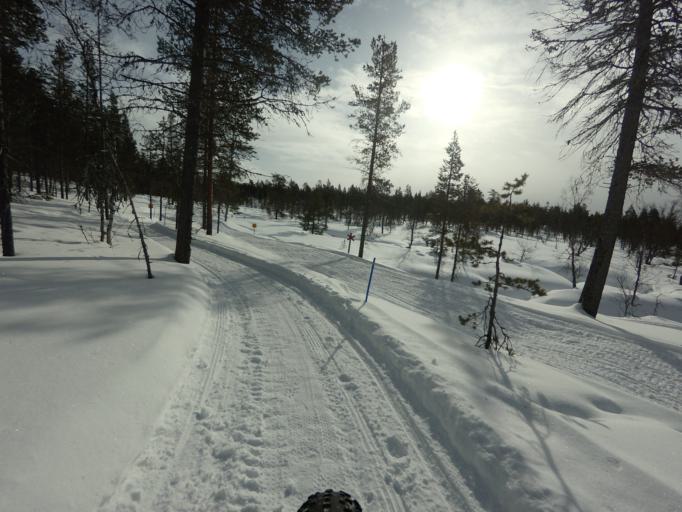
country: FI
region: Lapland
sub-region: Pohjois-Lappi
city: Ivalo
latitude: 68.3441
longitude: 27.4345
